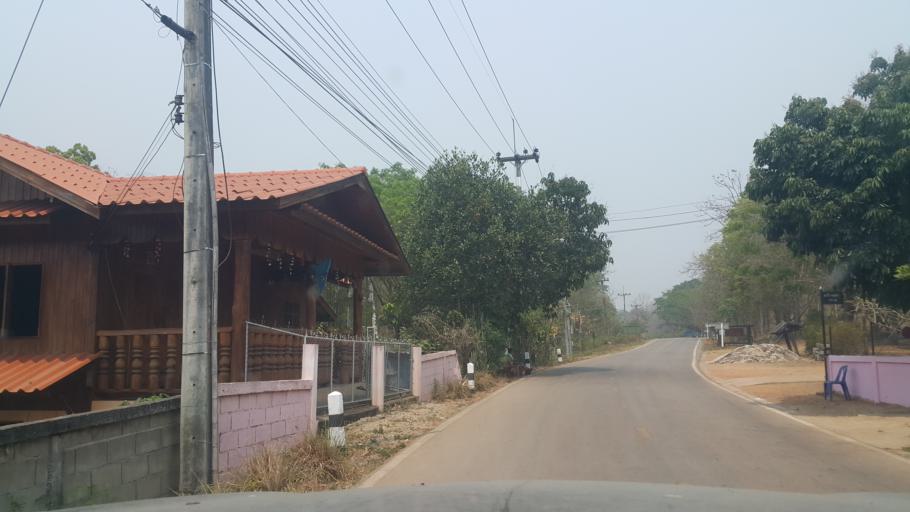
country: TH
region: Lampang
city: Soem Ngam
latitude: 18.1944
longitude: 99.1957
